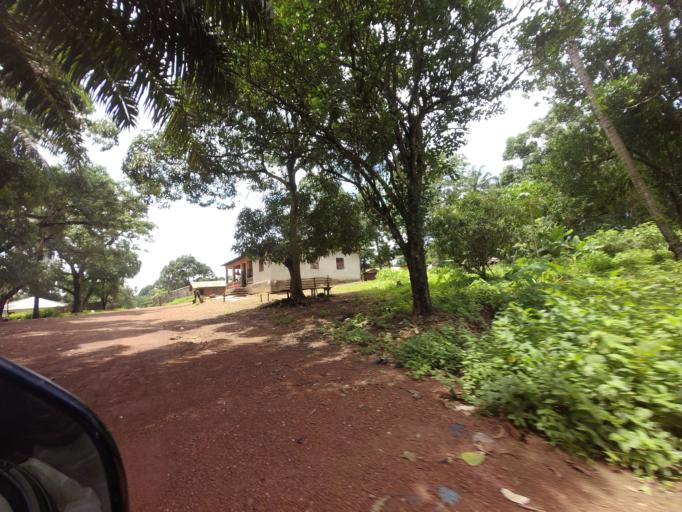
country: SL
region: Northern Province
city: Kambia
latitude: 9.1229
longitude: -12.9201
